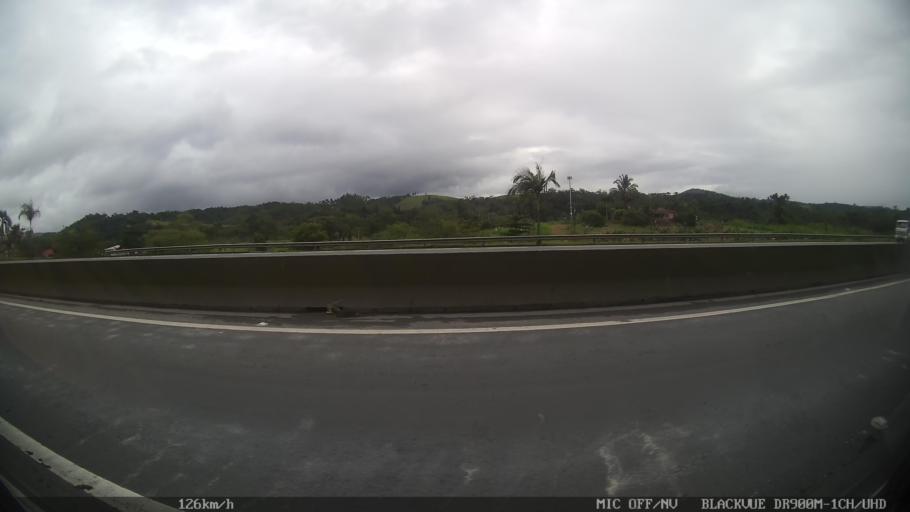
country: BR
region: Sao Paulo
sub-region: Cajati
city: Cajati
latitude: -24.7528
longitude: -48.1569
